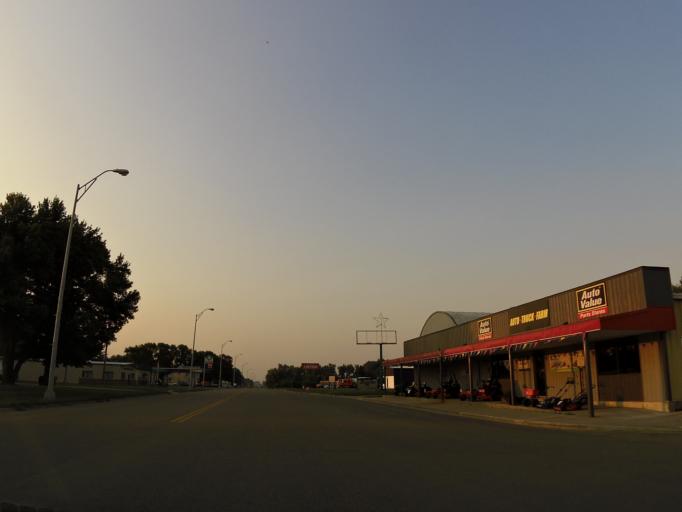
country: US
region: North Dakota
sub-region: Grand Forks County
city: Larimore
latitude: 47.9066
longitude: -97.6238
